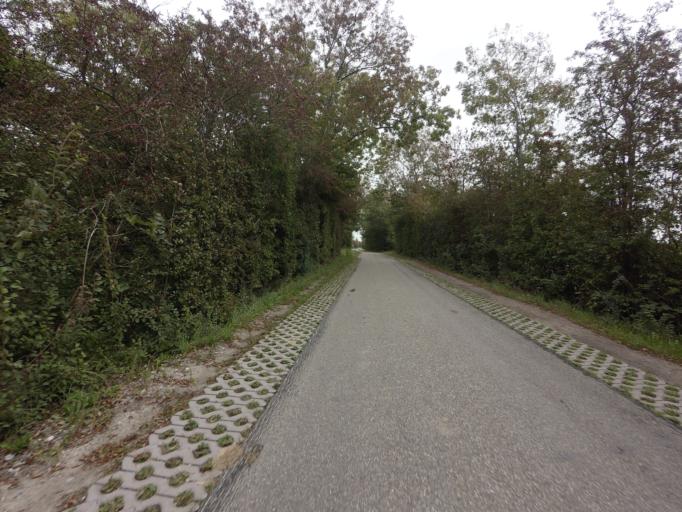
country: NL
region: Zeeland
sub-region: Gemeente Vlissingen
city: Vlissingen
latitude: 51.4905
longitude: 3.5626
